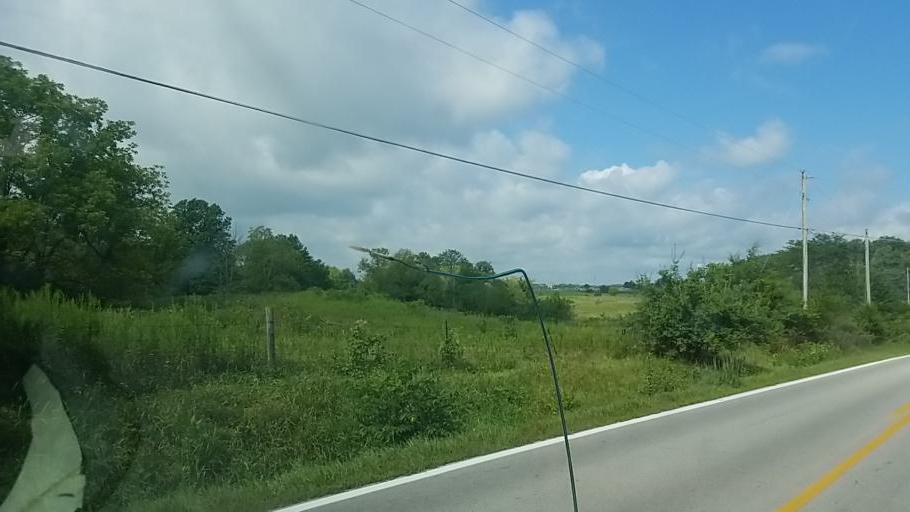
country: US
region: Ohio
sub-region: Pickaway County
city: Commercial Point
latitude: 39.8012
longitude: -83.1380
